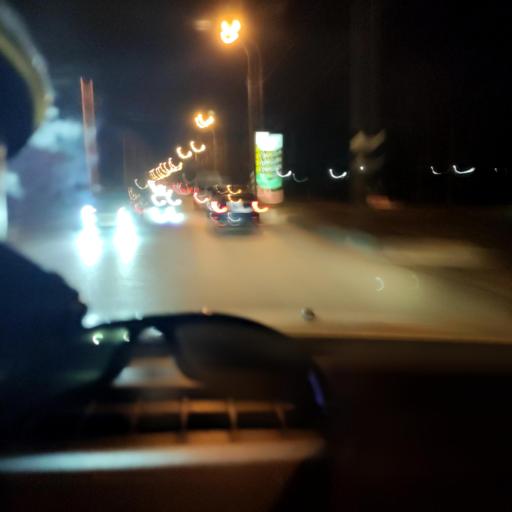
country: RU
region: Samara
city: Samara
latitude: 53.1492
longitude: 50.0943
